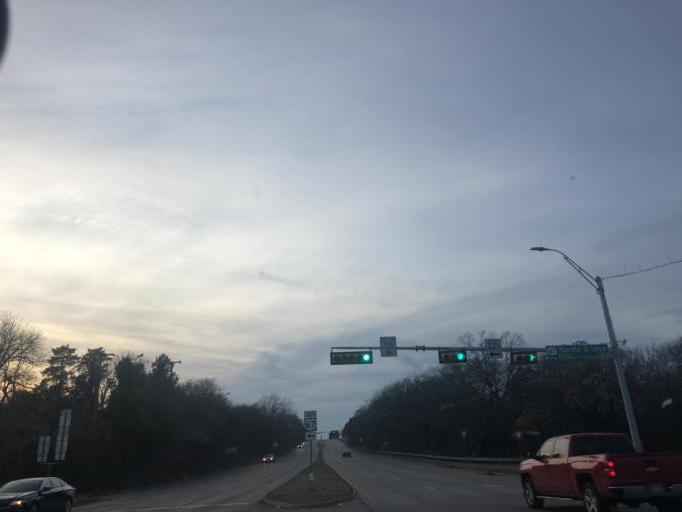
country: US
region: Texas
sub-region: Dallas County
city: Cockrell Hill
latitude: 32.6913
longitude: -96.8477
